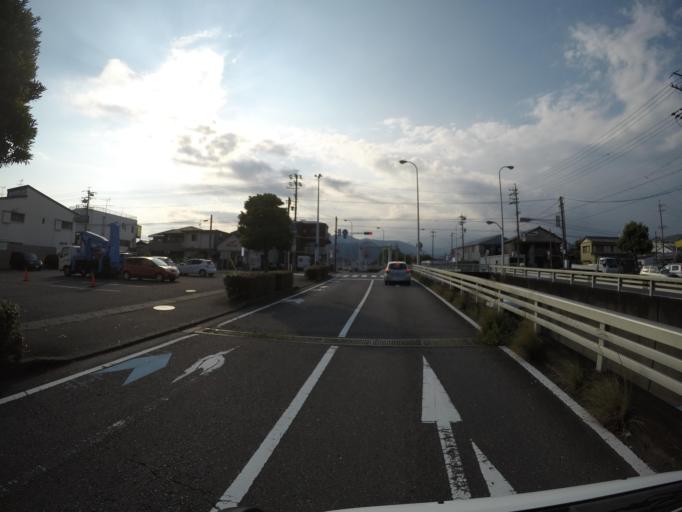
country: JP
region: Shizuoka
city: Shizuoka-shi
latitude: 35.0343
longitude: 138.4949
